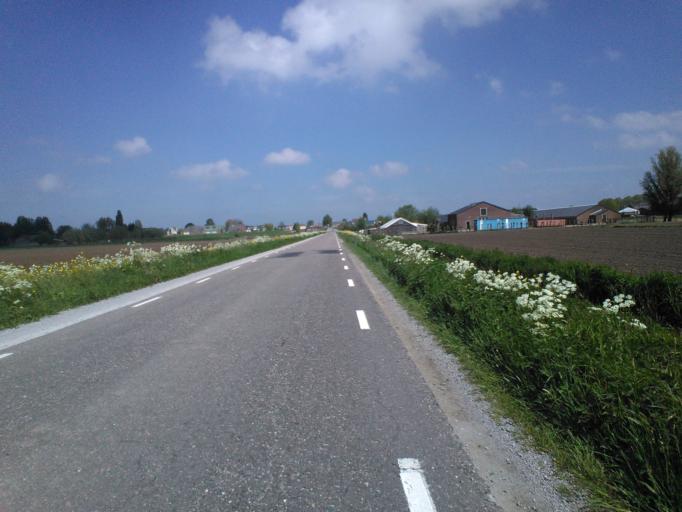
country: NL
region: South Holland
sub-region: Gemeente Boskoop
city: Boskoop
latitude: 52.0905
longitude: 4.6028
